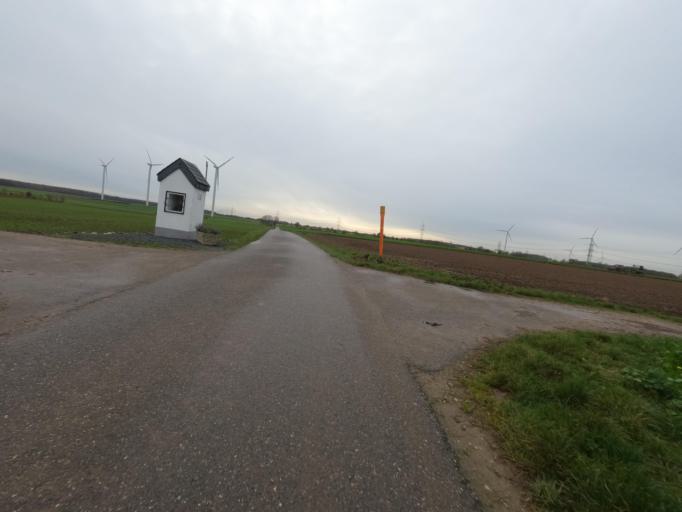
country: DE
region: North Rhine-Westphalia
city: Geilenkirchen
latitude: 51.0147
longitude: 6.1309
